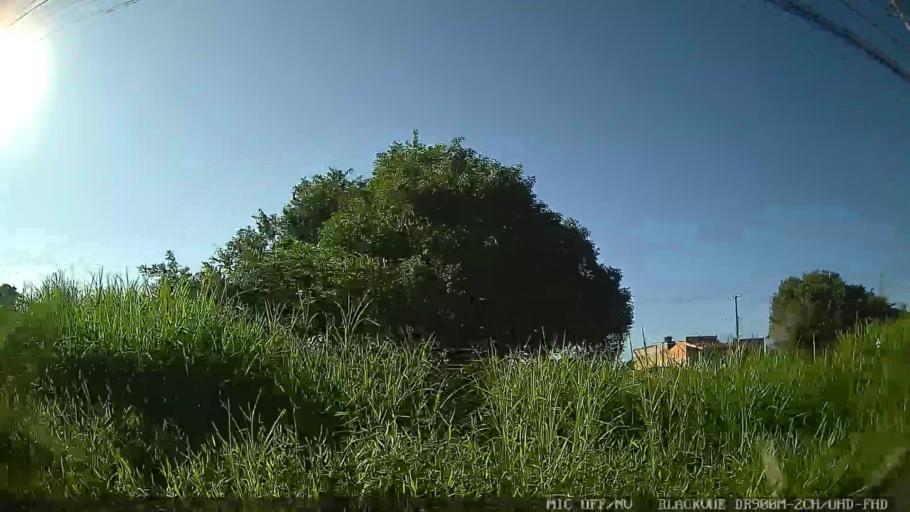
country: BR
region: Sao Paulo
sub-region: Peruibe
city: Peruibe
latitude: -24.2704
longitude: -46.9462
